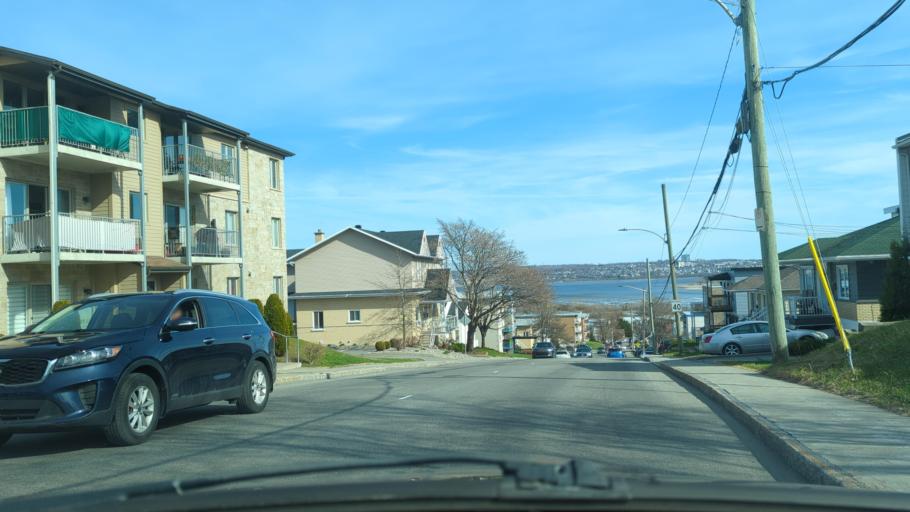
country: CA
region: Quebec
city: Quebec
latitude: 46.8567
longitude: -71.2075
